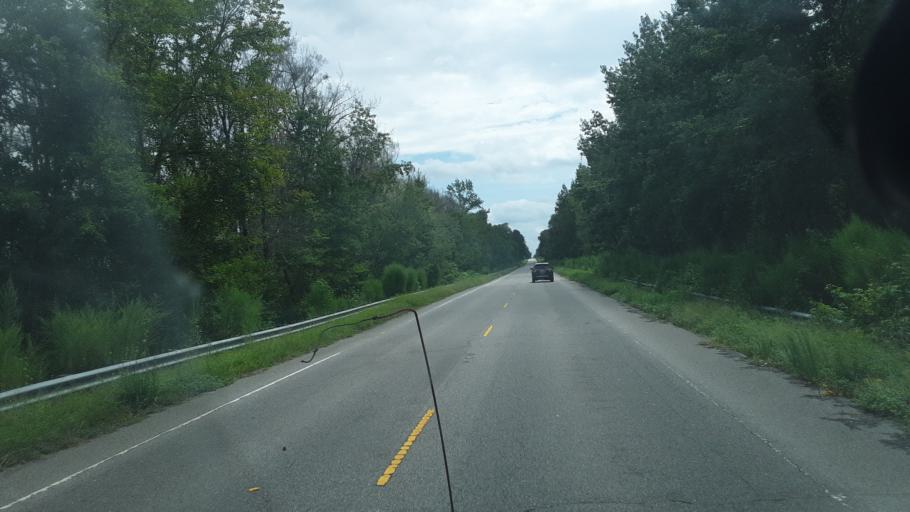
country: US
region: North Carolina
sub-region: Robeson County
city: Maxton
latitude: 34.6530
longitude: -79.3744
